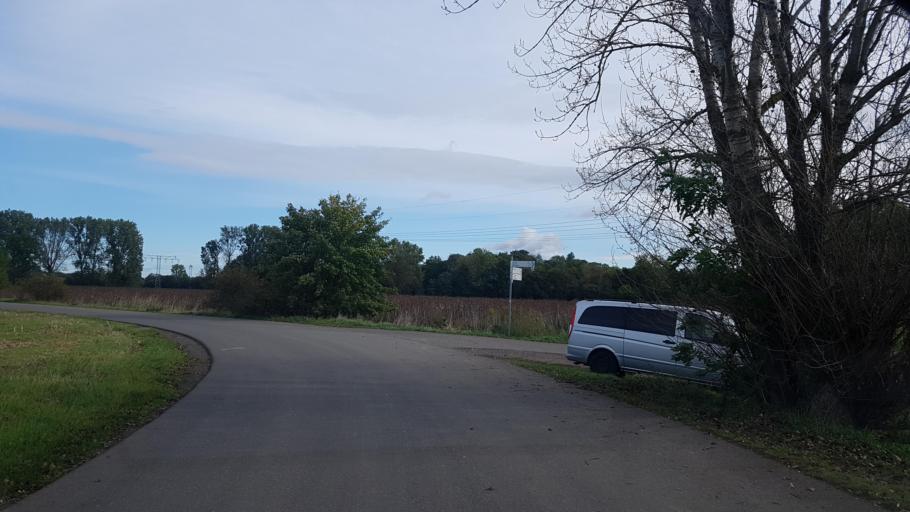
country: DE
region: Saxony
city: Groitzsch
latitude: 51.1572
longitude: 12.2678
